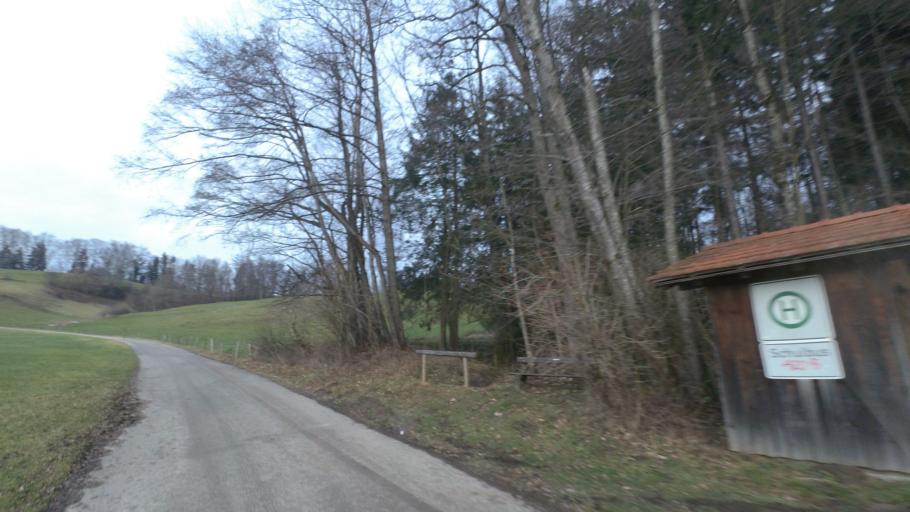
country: DE
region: Bavaria
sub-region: Upper Bavaria
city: Ubersee
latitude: 47.8078
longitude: 12.5079
